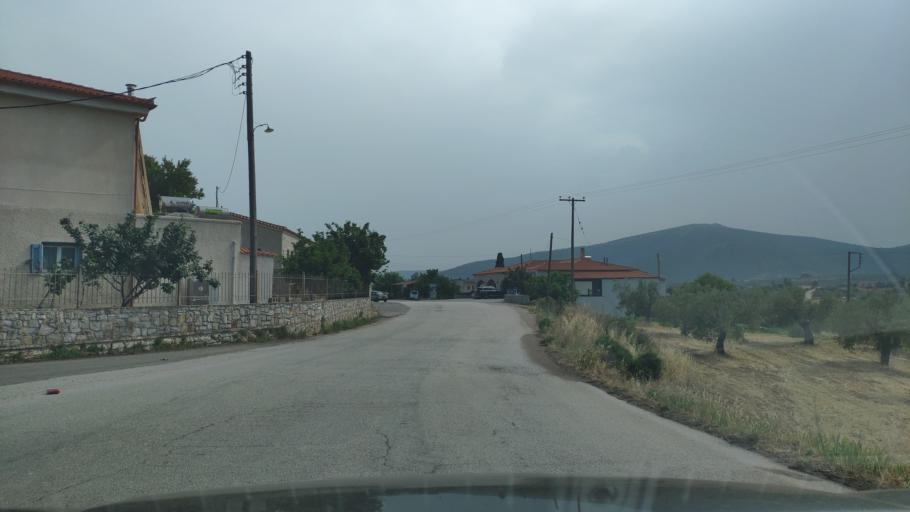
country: GR
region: Peloponnese
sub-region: Nomos Argolidos
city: Palaia Epidavros
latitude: 37.5947
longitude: 23.1588
